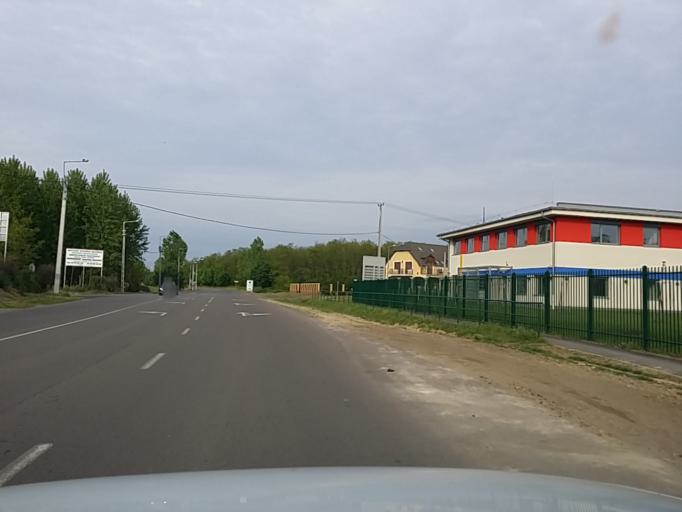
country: HU
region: Heves
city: Boldog
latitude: 47.5819
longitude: 19.7402
